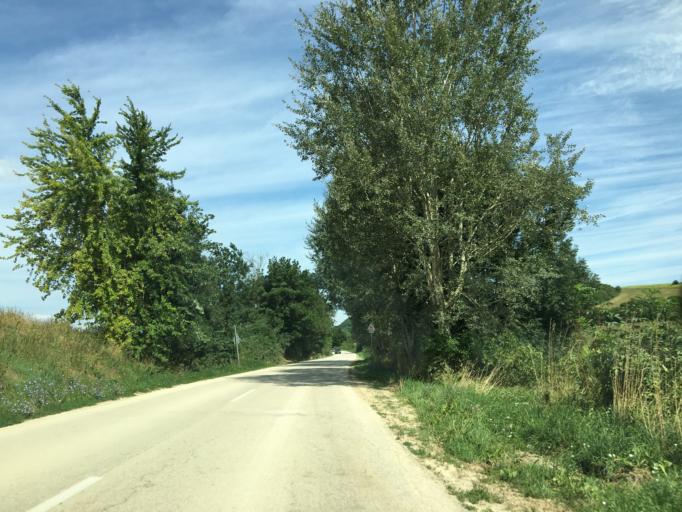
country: HU
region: Komarom-Esztergom
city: Bajna
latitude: 47.6233
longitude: 18.6273
